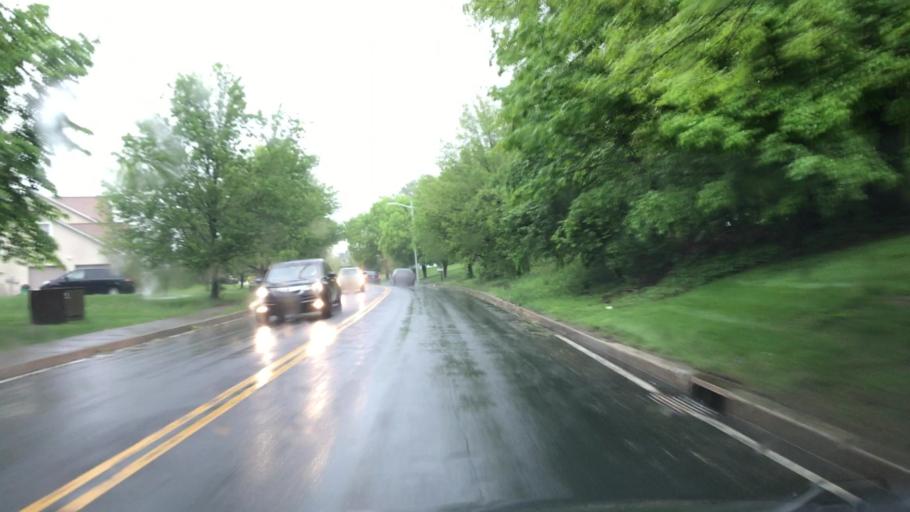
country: US
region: New York
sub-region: Rockland County
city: Hillcrest
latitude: 41.1182
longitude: -74.0254
